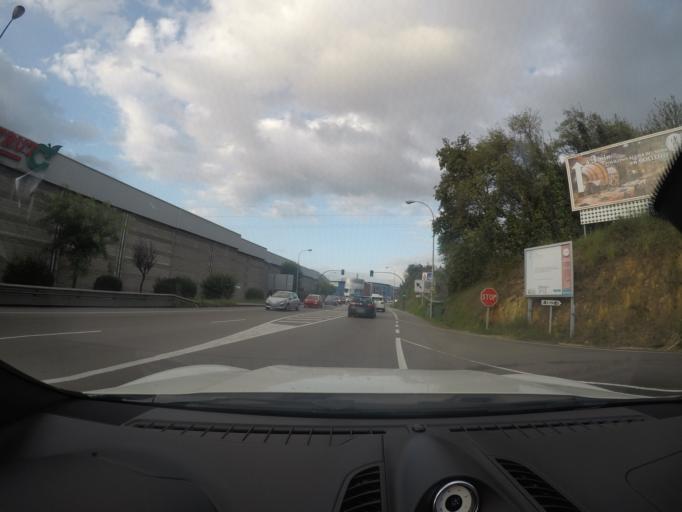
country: ES
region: Asturias
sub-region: Province of Asturias
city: Lugones
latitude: 43.3730
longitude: -5.8116
